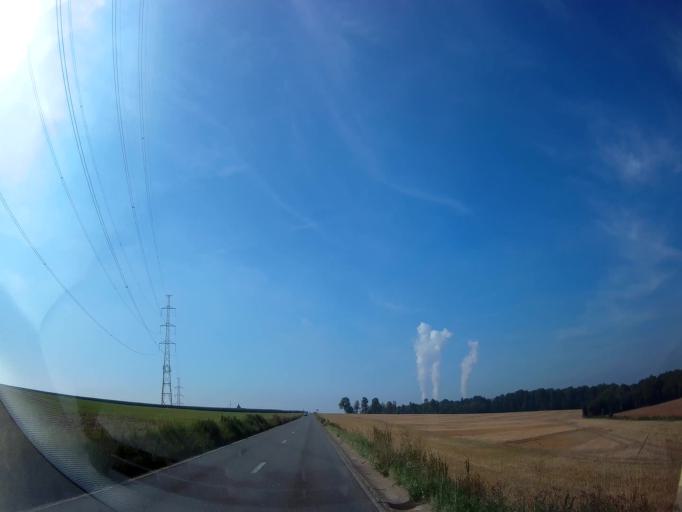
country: BE
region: Wallonia
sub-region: Province de Liege
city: Verlaine
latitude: 50.5838
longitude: 5.3343
